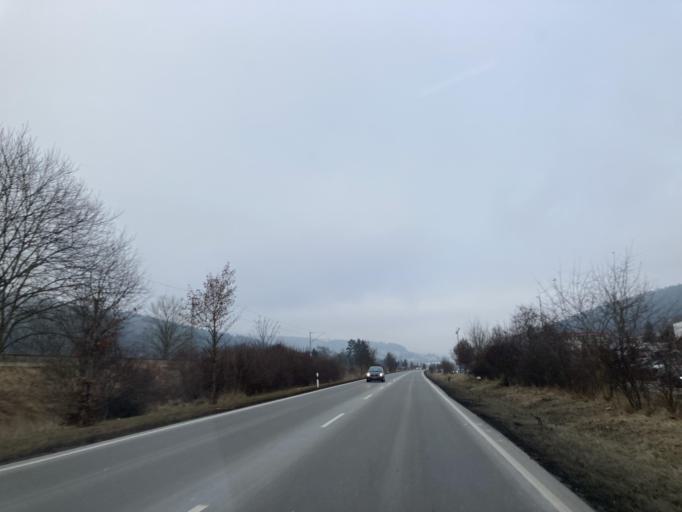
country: DE
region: Baden-Wuerttemberg
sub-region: Freiburg Region
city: Wurmlingen
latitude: 47.9679
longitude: 8.7857
